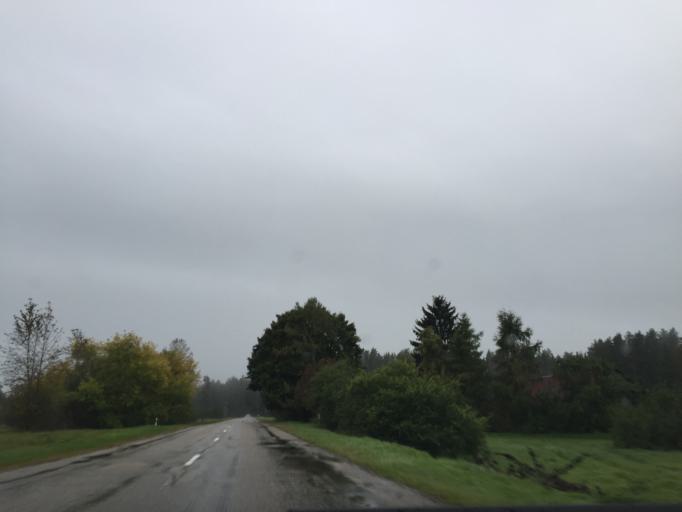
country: LV
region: Incukalns
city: Incukalns
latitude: 57.0680
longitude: 24.6683
